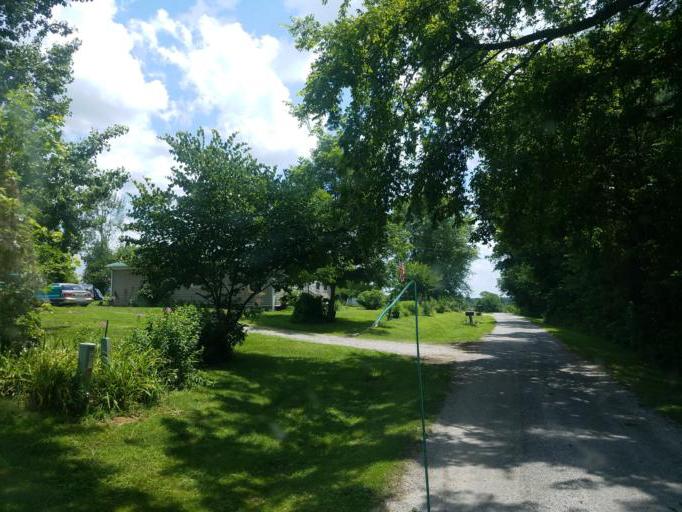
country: US
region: Kentucky
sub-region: Grayson County
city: Leitchfield
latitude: 37.4828
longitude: -86.4696
